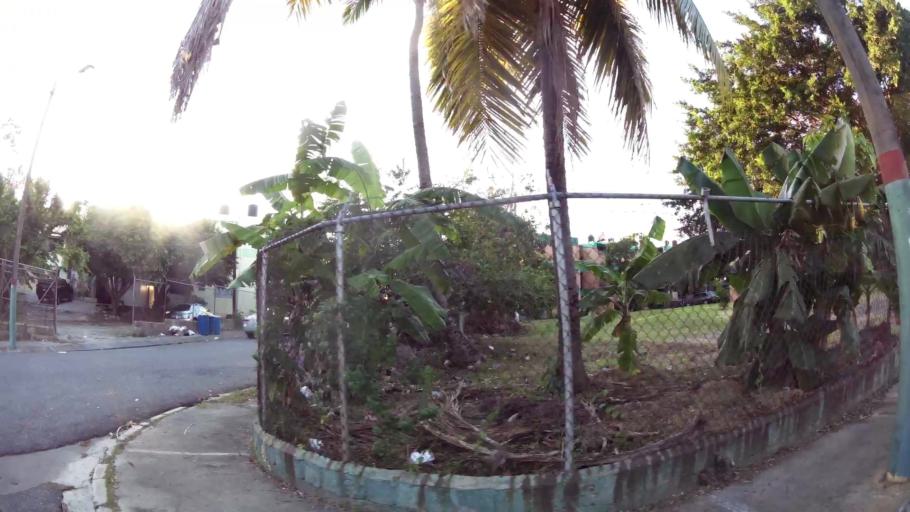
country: DO
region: Nacional
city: La Agustina
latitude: 18.4867
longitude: -69.9594
